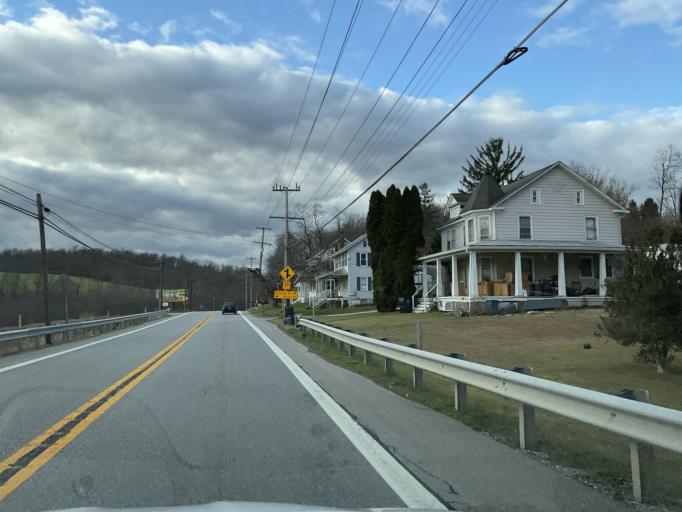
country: US
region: Pennsylvania
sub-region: Adams County
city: Mount Pleasant
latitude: 39.6710
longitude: -77.0282
